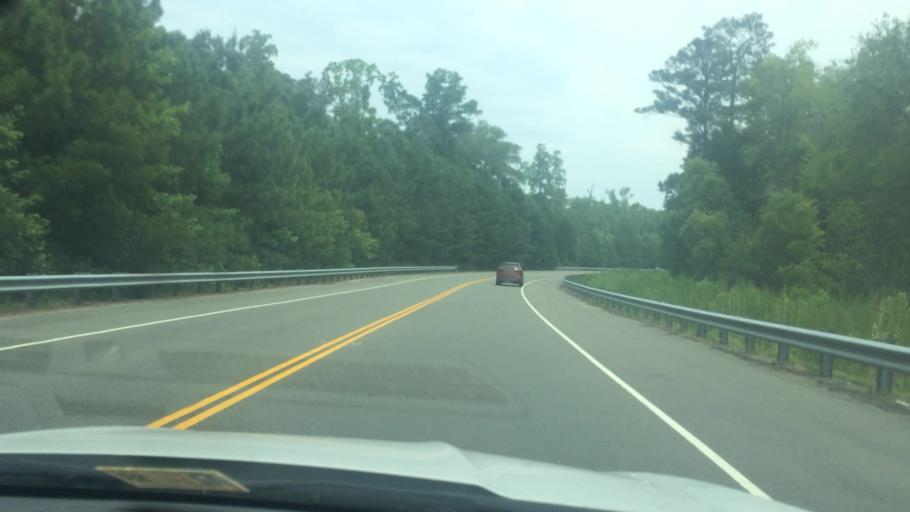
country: US
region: Virginia
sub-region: James City County
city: Williamsburg
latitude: 37.2660
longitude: -76.7755
